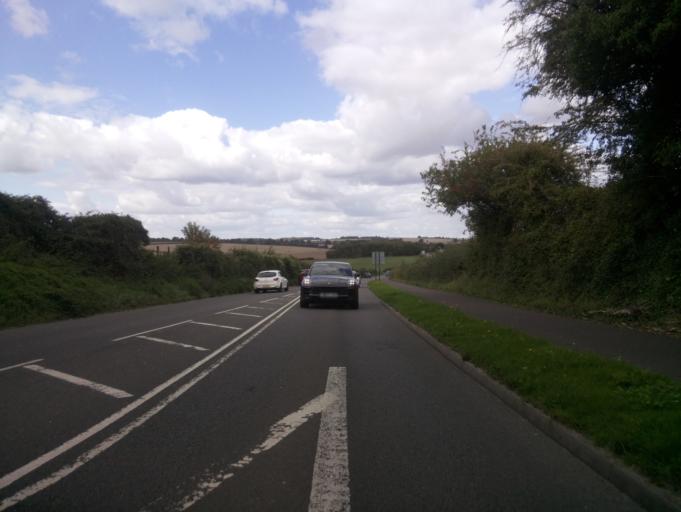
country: GB
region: England
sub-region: Wiltshire
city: Salisbury
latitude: 51.0938
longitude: -1.7995
